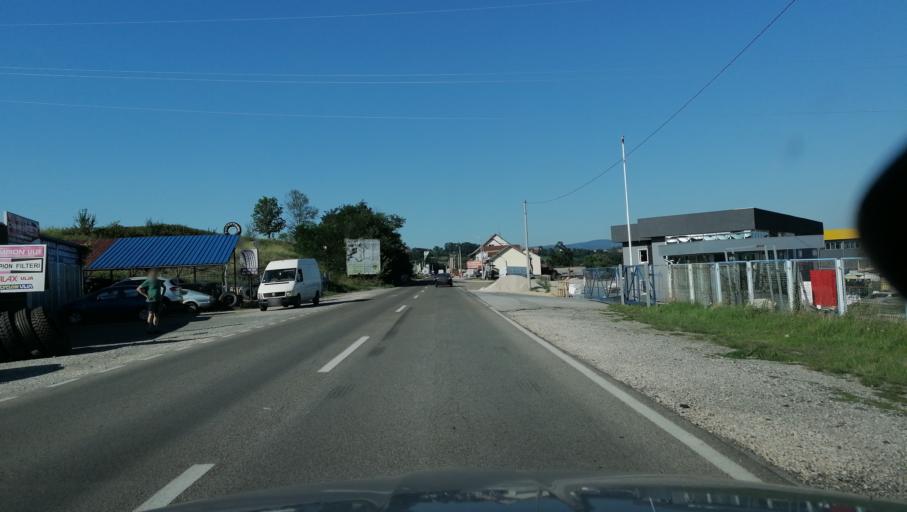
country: RS
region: Central Serbia
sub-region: Raski Okrug
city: Kraljevo
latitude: 43.7078
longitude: 20.6151
